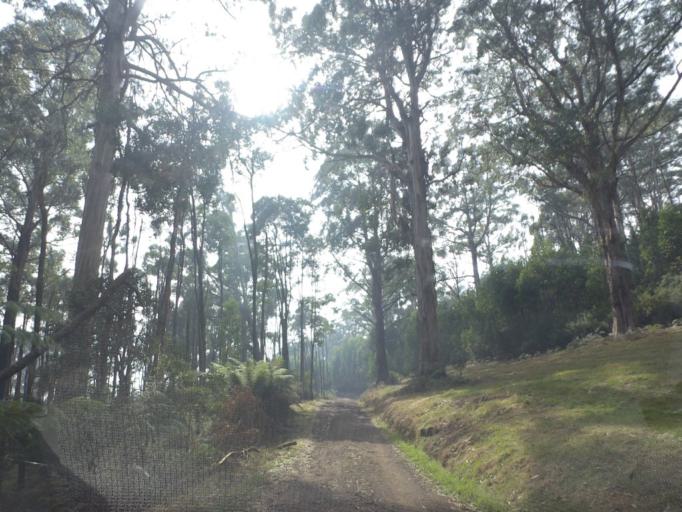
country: AU
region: Victoria
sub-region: Yarra Ranges
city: Healesville
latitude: -37.5662
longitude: 145.5880
